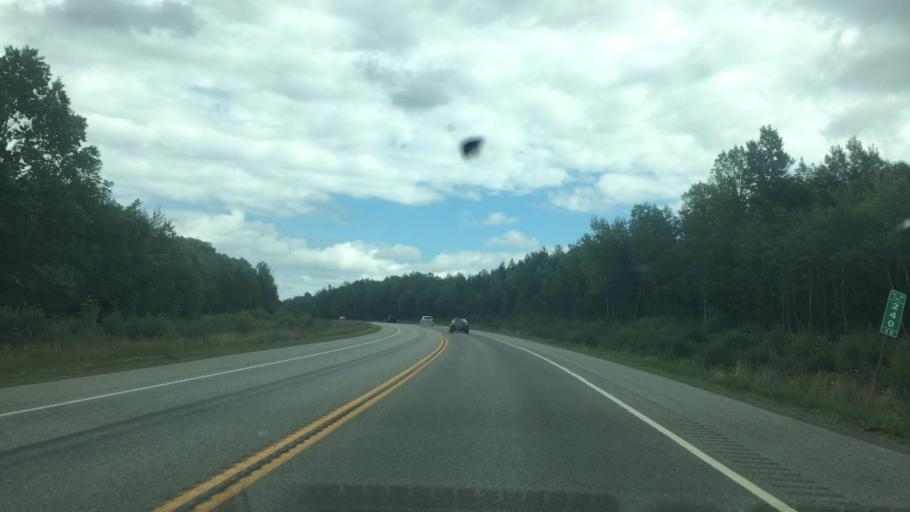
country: CA
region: Nova Scotia
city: Antigonish
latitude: 45.5886
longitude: -61.7714
